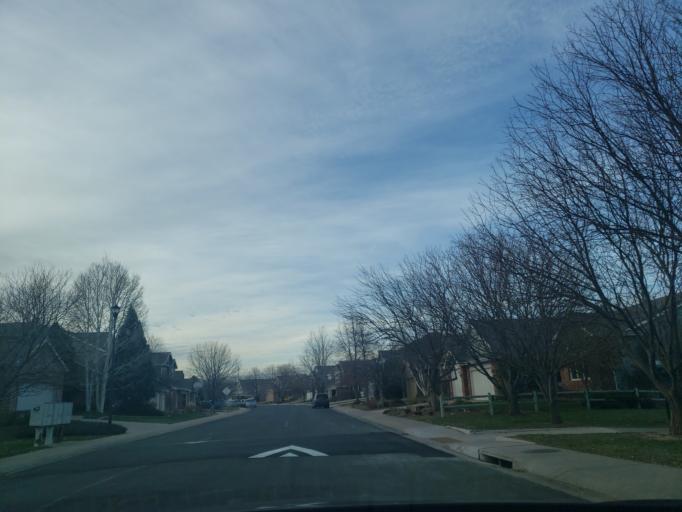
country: US
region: Colorado
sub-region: Larimer County
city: Fort Collins
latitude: 40.5097
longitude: -105.0439
